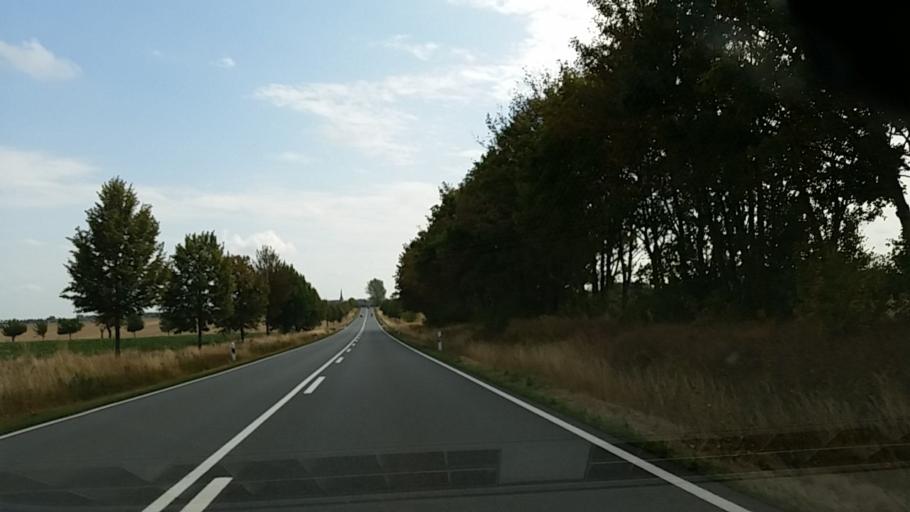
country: DE
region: Saxony-Anhalt
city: Nemsdorf-Gohrendorf
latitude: 51.3572
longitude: 11.6257
